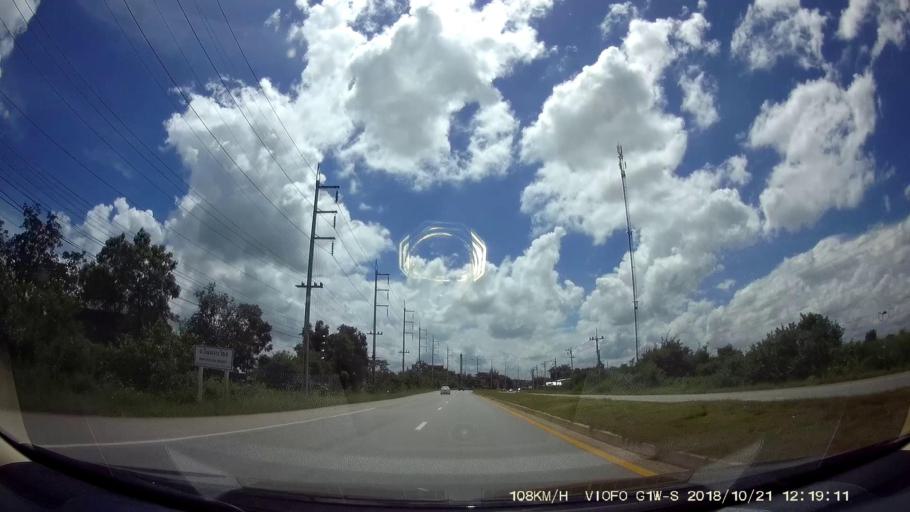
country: TH
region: Nakhon Ratchasima
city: Dan Khun Thot
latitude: 15.3046
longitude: 101.8149
